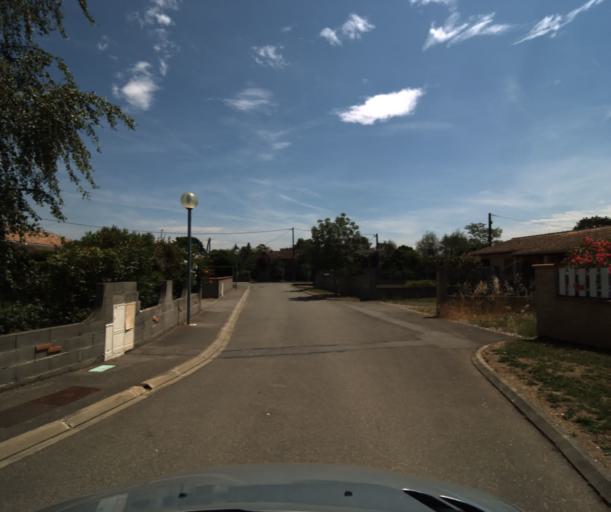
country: FR
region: Midi-Pyrenees
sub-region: Departement de la Haute-Garonne
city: Labastidette
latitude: 43.4646
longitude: 1.2481
